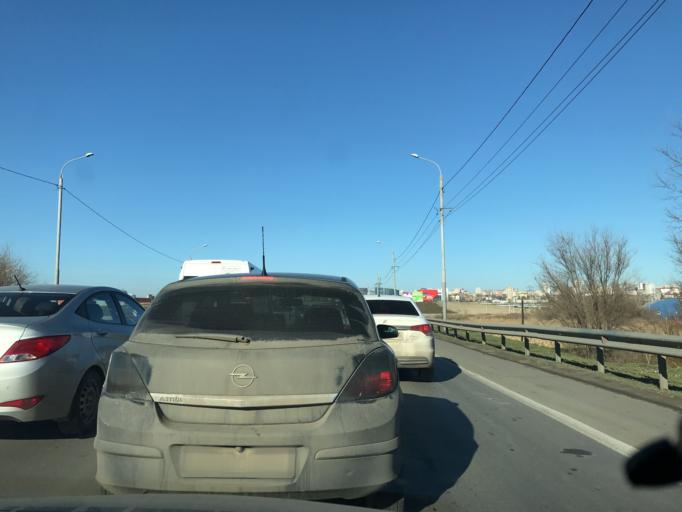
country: RU
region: Rostov
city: Rostov-na-Donu
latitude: 47.1998
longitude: 39.7300
